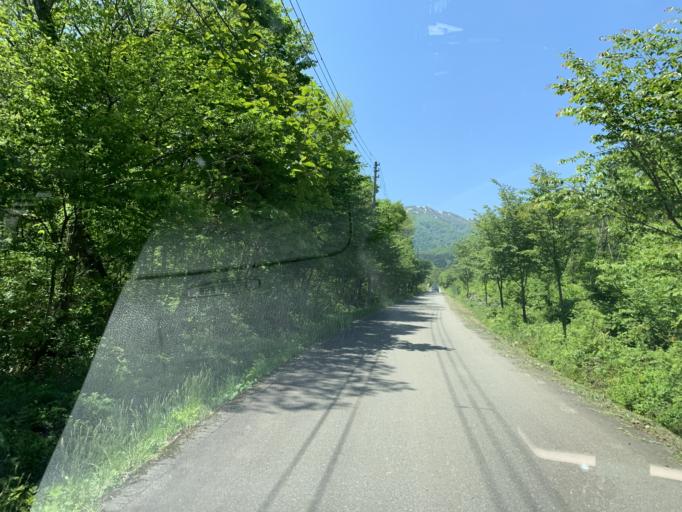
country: JP
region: Iwate
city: Shizukuishi
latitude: 39.5455
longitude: 140.8235
